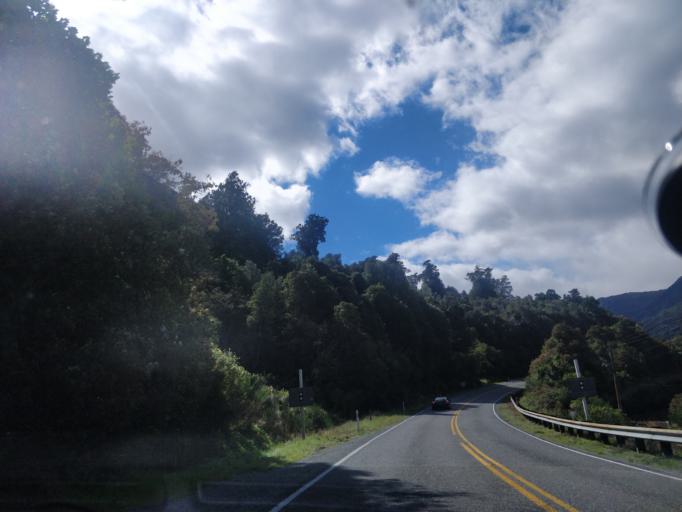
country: NZ
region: West Coast
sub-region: Grey District
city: Greymouth
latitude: -42.7962
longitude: 171.5827
